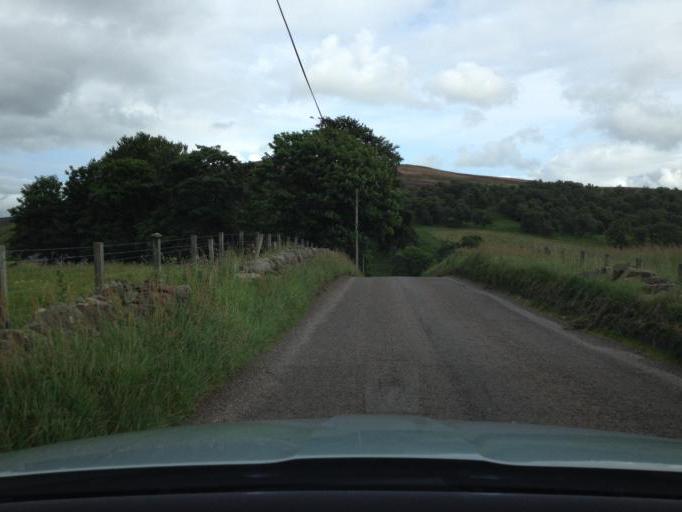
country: GB
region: Scotland
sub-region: Angus
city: Brechin
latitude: 56.8606
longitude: -2.6859
